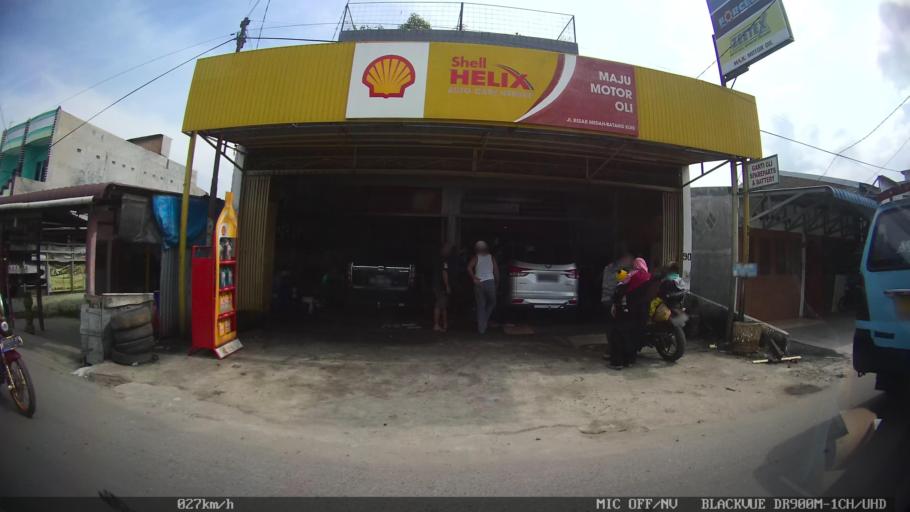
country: ID
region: North Sumatra
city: Medan
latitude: 3.6071
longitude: 98.7617
